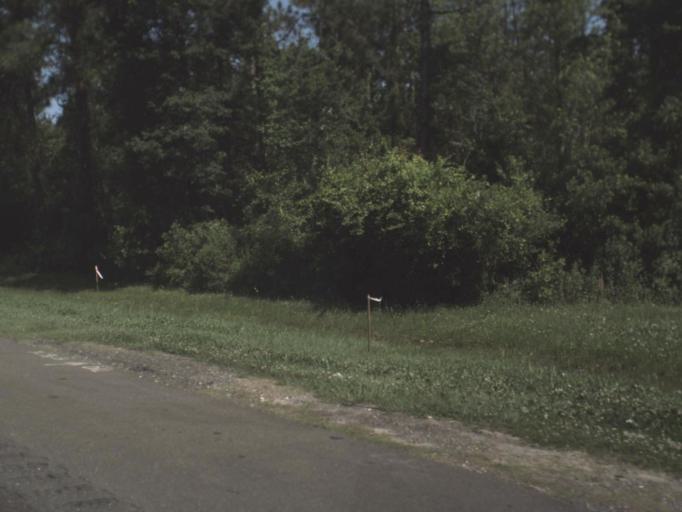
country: US
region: Florida
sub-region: Duval County
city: Baldwin
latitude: 30.3060
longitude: -81.8828
